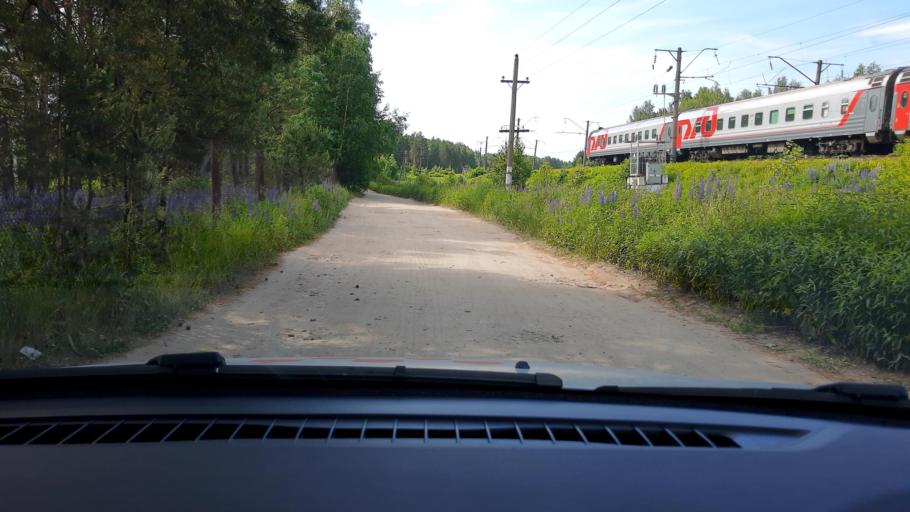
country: RU
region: Nizjnij Novgorod
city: Linda
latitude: 56.6634
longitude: 44.1687
